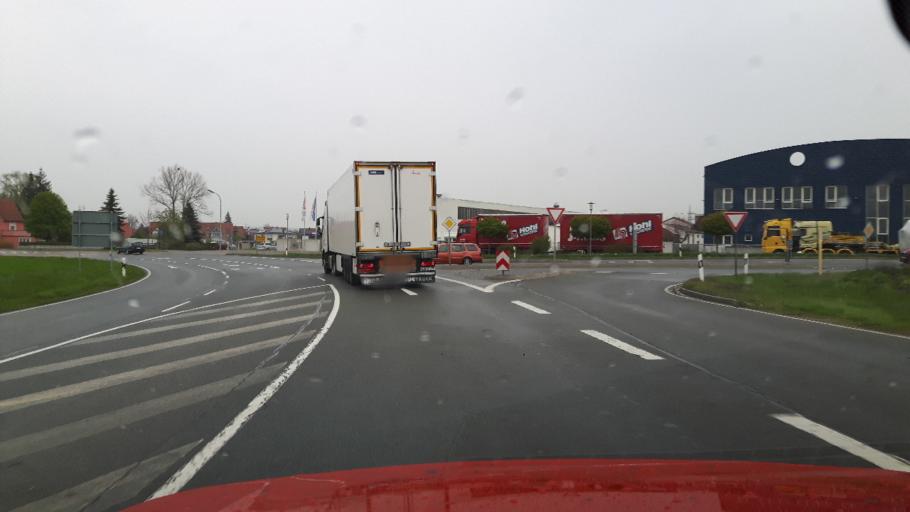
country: DE
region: Bavaria
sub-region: Regierungsbezirk Mittelfranken
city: Gunzenhausen
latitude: 49.1248
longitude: 10.7505
